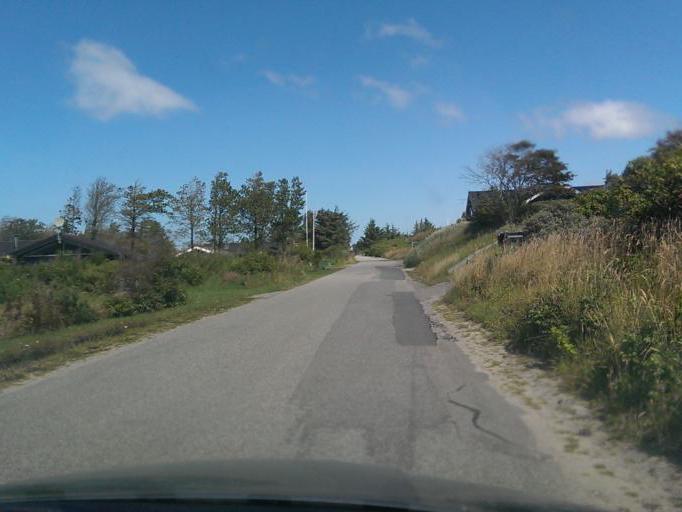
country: DK
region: North Denmark
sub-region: Jammerbugt Kommune
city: Pandrup
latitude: 57.2540
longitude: 9.5935
